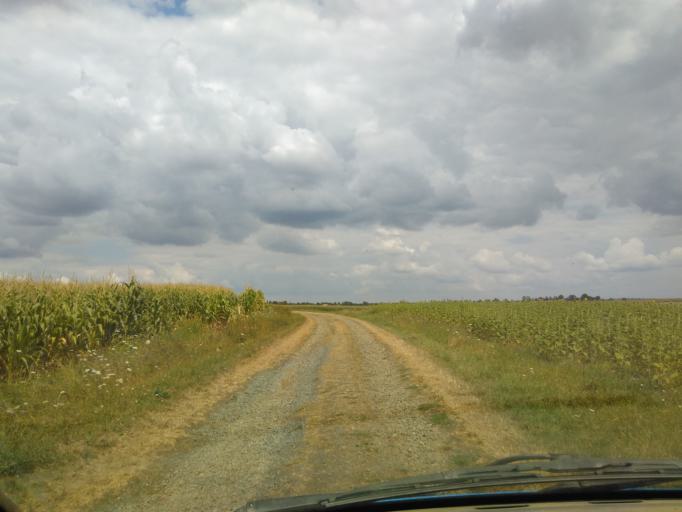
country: FR
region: Pays de la Loire
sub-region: Departement de la Vendee
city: Sainte-Hermine
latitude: 46.5635
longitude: -1.0248
